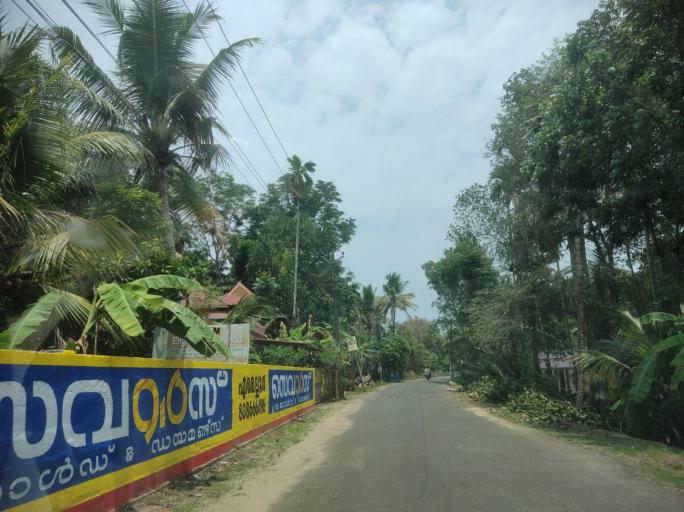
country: IN
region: Kerala
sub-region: Alappuzha
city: Vayalar
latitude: 9.7489
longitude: 76.3249
